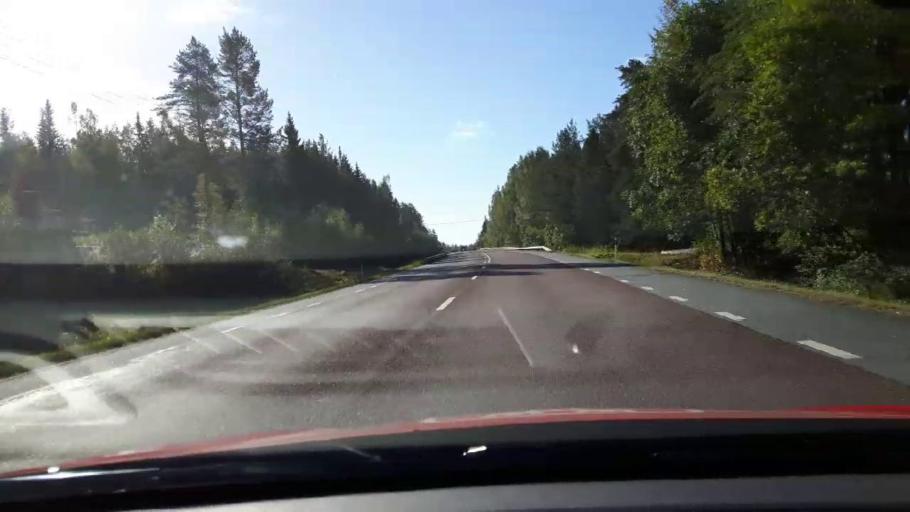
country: SE
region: Jaemtland
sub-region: Braecke Kommun
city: Braecke
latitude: 62.7937
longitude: 15.3753
